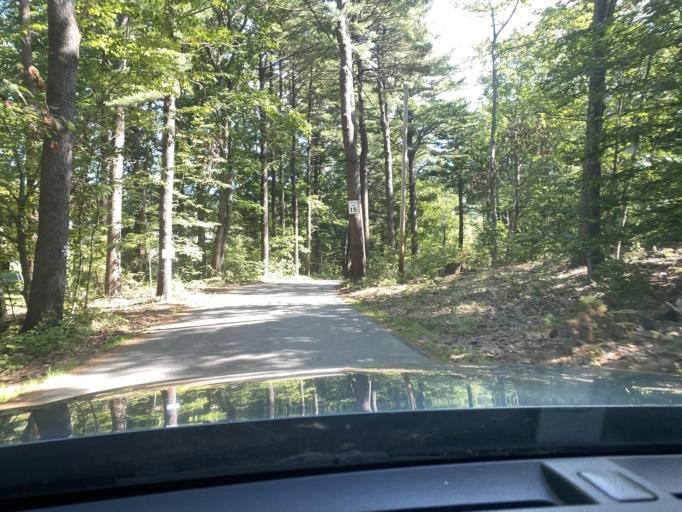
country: US
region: New Hampshire
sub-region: Rockingham County
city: Portsmouth
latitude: 43.0560
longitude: -70.7573
